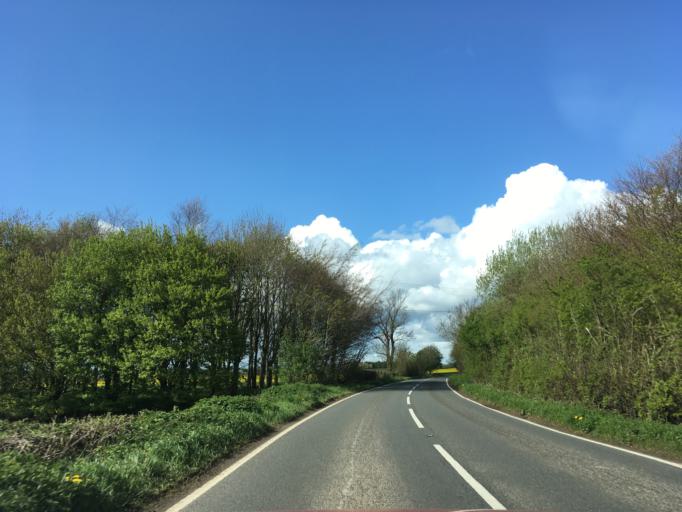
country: GB
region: England
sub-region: Gloucestershire
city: Tetbury
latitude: 51.6647
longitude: -2.1794
